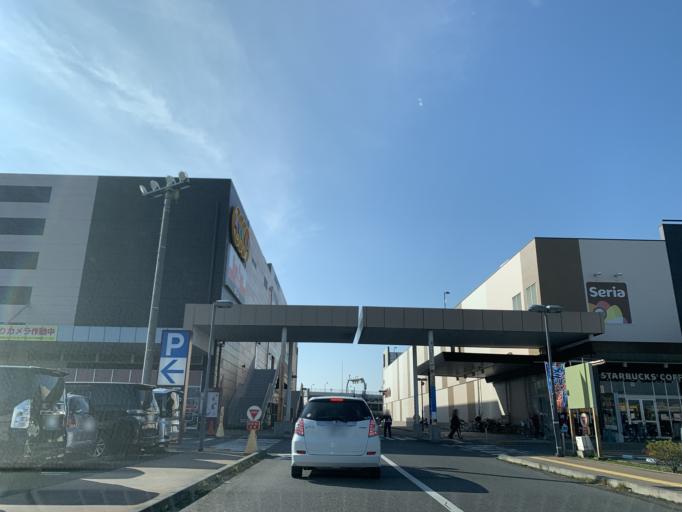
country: JP
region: Saitama
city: Yashio-shi
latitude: 35.8427
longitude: 139.8555
